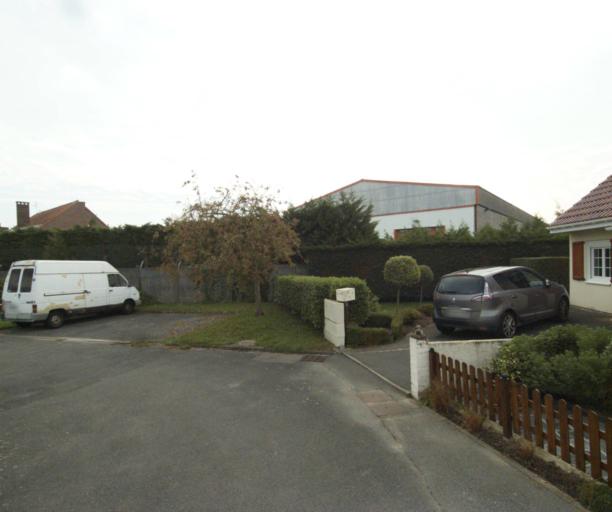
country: FR
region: Nord-Pas-de-Calais
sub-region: Departement du Nord
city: Seclin
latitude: 50.5396
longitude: 3.0231
